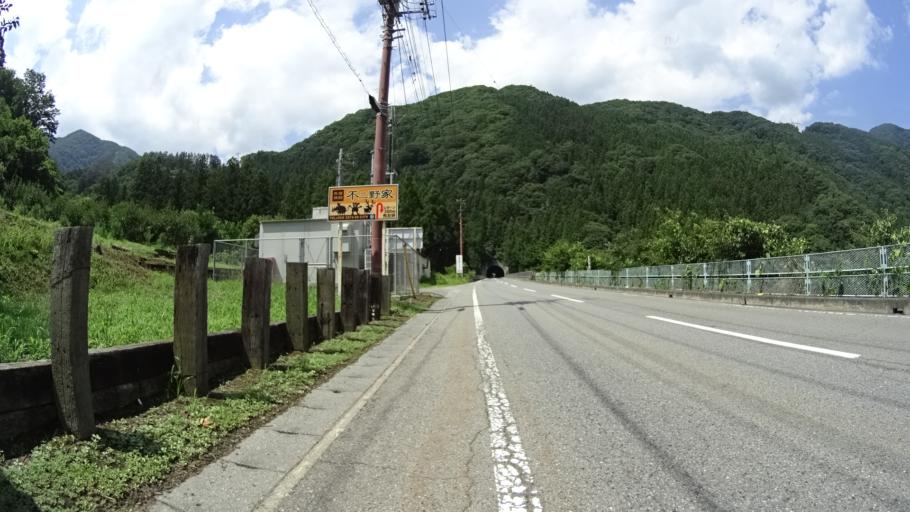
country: JP
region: Gunma
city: Tomioka
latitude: 36.0826
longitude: 138.7709
